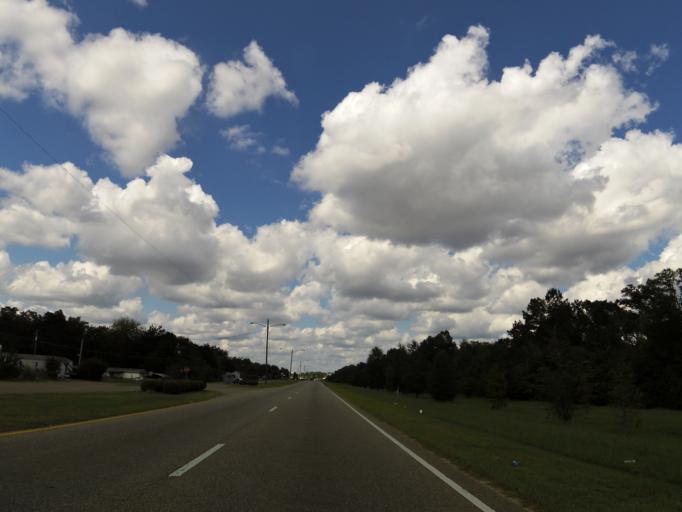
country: US
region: Alabama
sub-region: Dallas County
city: Selmont-West Selmont
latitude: 32.3901
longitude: -87.0131
